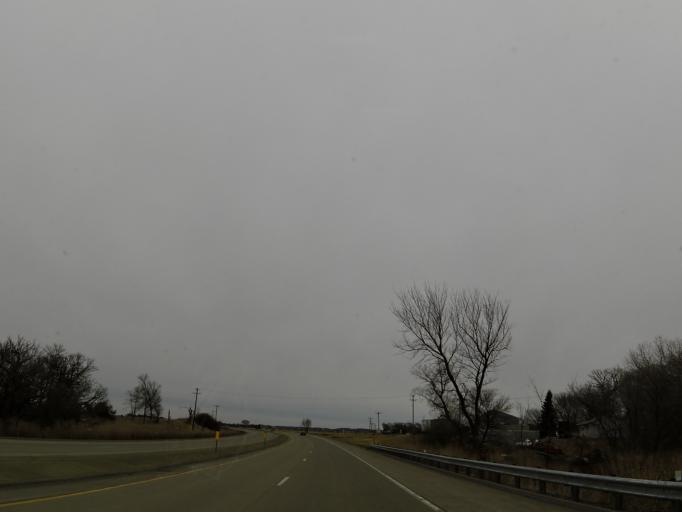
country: US
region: Minnesota
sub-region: Scott County
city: Belle Plaine
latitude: 44.6013
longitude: -93.7911
